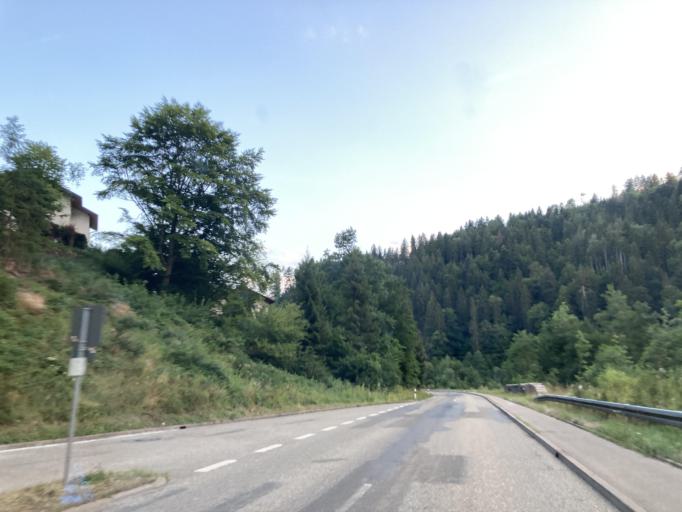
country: DE
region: Baden-Wuerttemberg
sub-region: Freiburg Region
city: Dornhan
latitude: 48.3800
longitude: 8.5396
